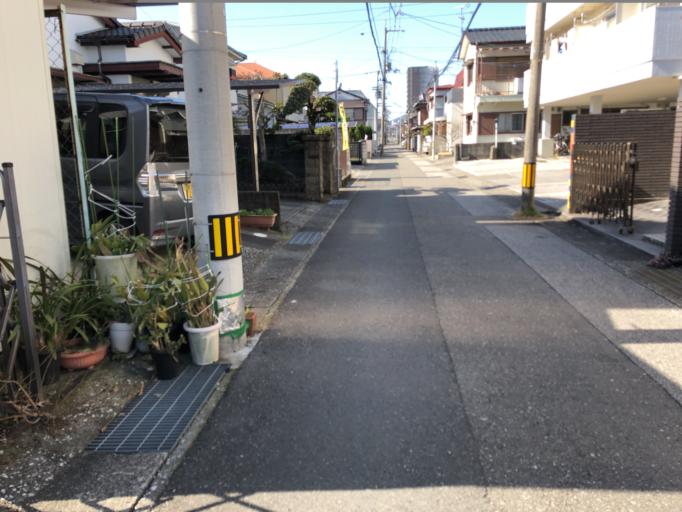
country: JP
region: Kochi
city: Kochi-shi
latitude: 33.5608
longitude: 133.5525
